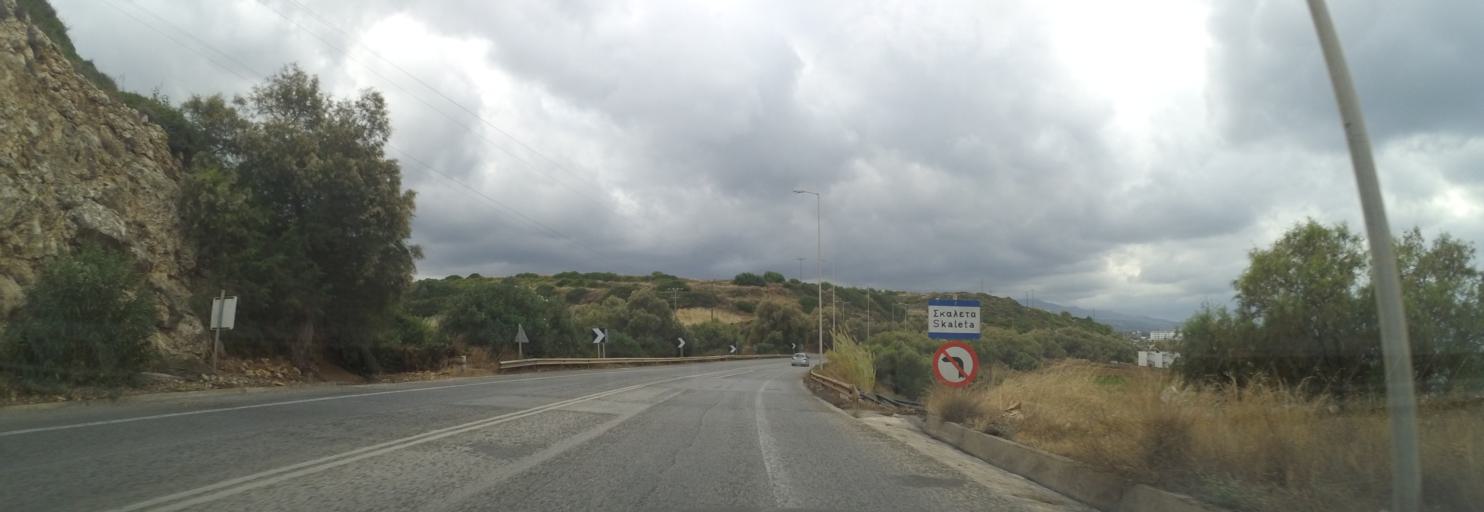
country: GR
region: Crete
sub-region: Nomos Rethymnis
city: Panormos
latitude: 35.3945
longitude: 24.6175
